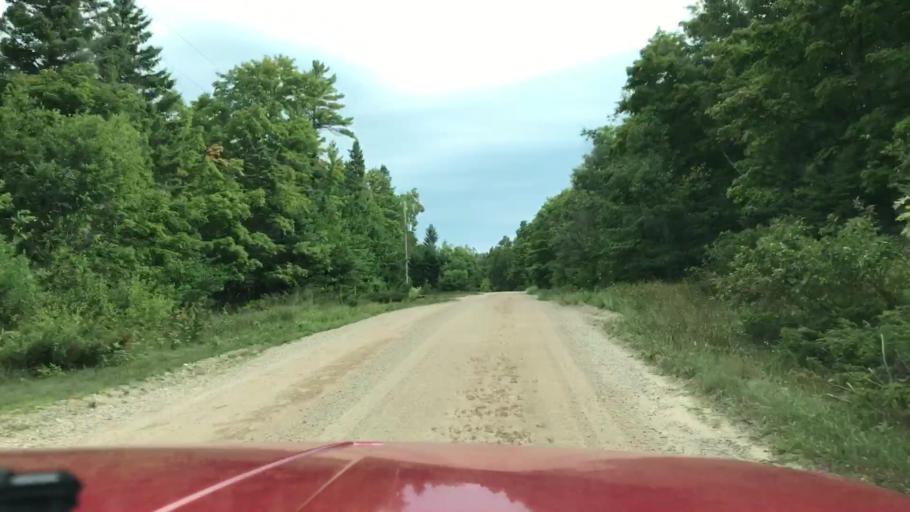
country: US
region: Michigan
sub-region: Charlevoix County
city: Charlevoix
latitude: 45.7309
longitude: -85.5642
